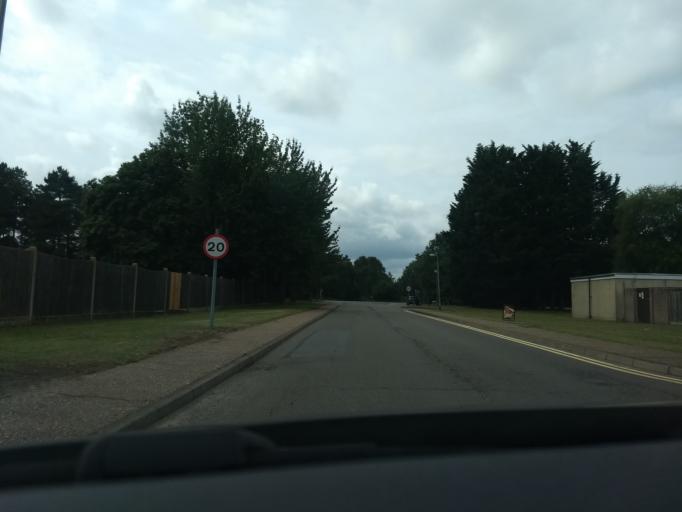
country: GB
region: England
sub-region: Suffolk
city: Woodbridge
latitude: 52.0808
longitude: 1.3873
